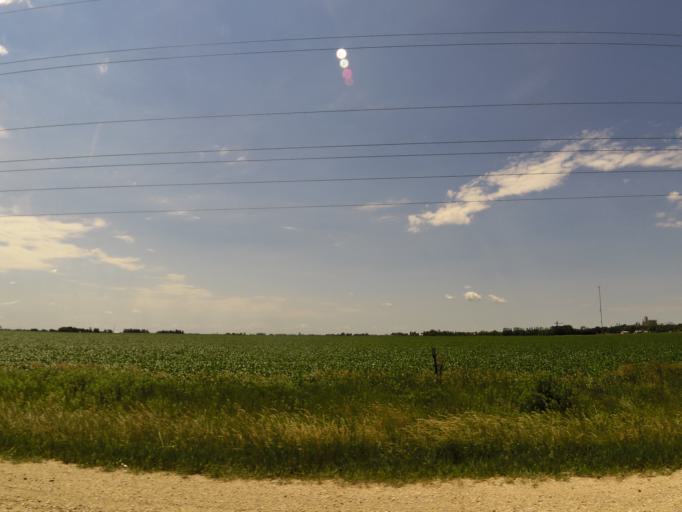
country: US
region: Iowa
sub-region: Bremer County
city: Tripoli
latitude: 42.7148
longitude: -92.2123
